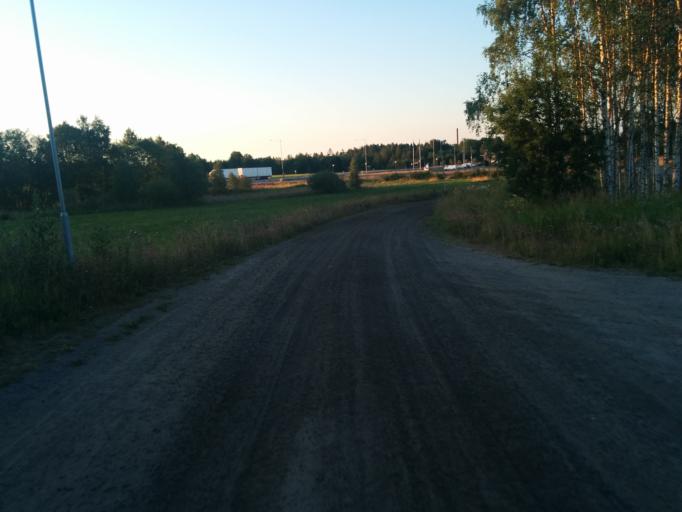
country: SE
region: Vaesterbotten
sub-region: Umea Kommun
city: Ersmark
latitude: 63.8527
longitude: 20.3796
